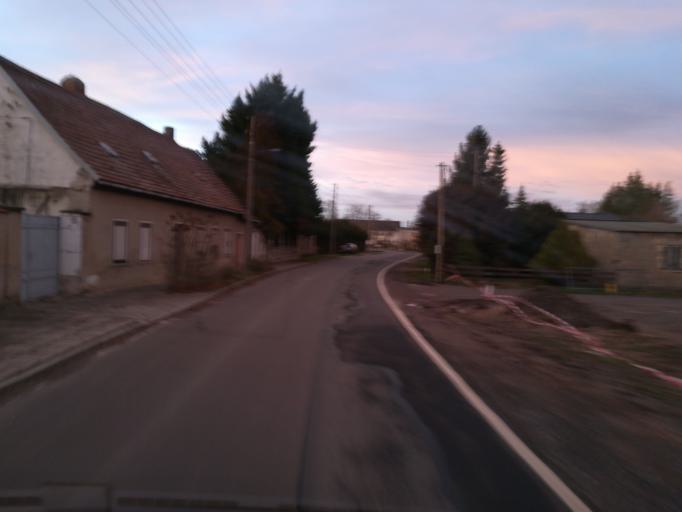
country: DE
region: Saxony-Anhalt
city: Brehna
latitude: 51.5373
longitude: 12.2284
